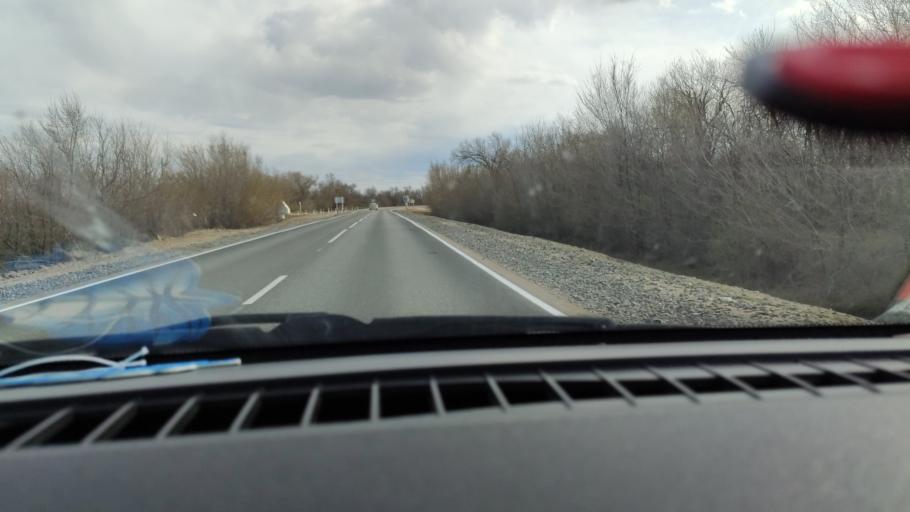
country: RU
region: Saratov
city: Krasnoarmeysk
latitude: 51.1060
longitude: 45.9571
